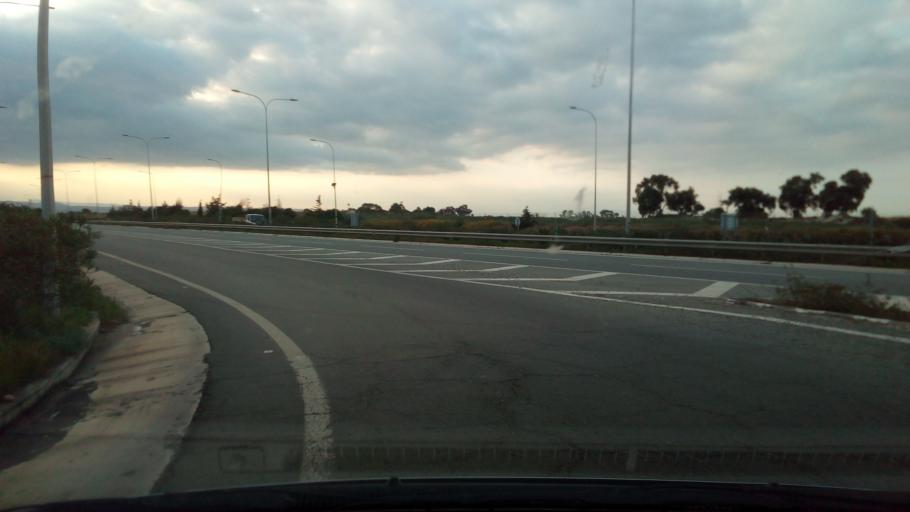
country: CY
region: Ammochostos
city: Avgorou
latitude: 34.9721
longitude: 33.8283
